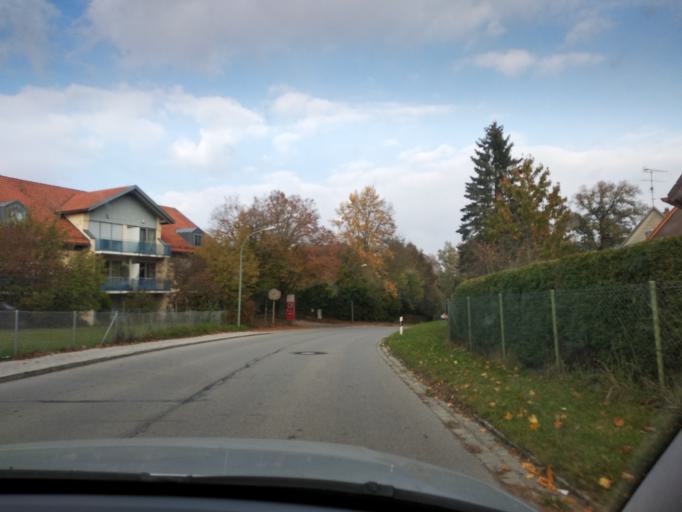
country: DE
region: Bavaria
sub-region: Upper Bavaria
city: Ottenhofen
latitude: 48.2133
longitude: 11.8788
